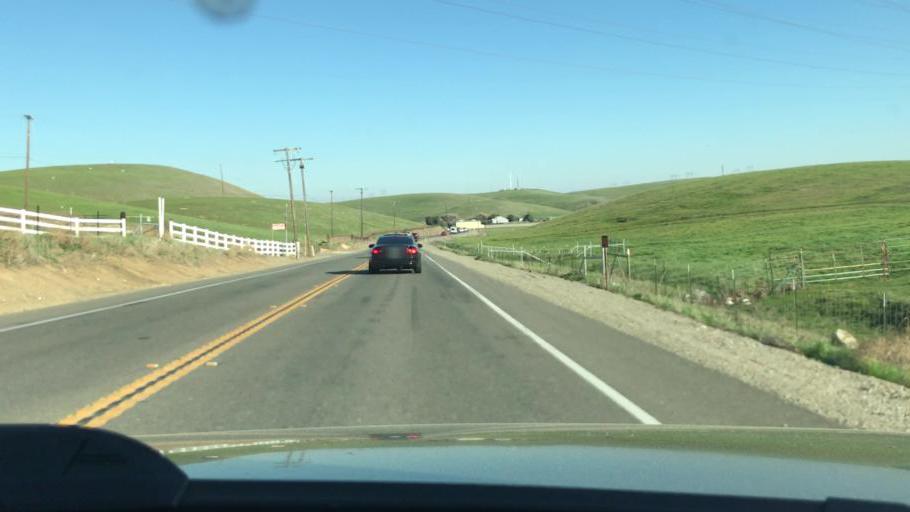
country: US
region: California
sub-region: San Joaquin County
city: Mountain House
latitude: 37.7448
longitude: -121.5973
